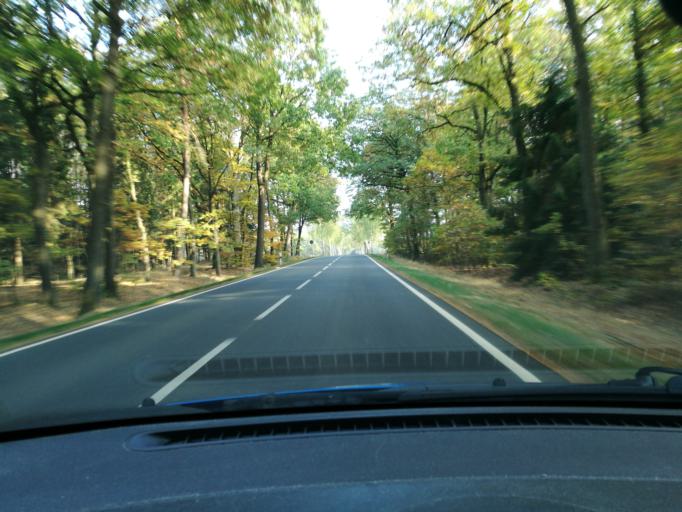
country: DE
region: Lower Saxony
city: Gohrde
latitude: 53.1282
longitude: 10.9106
